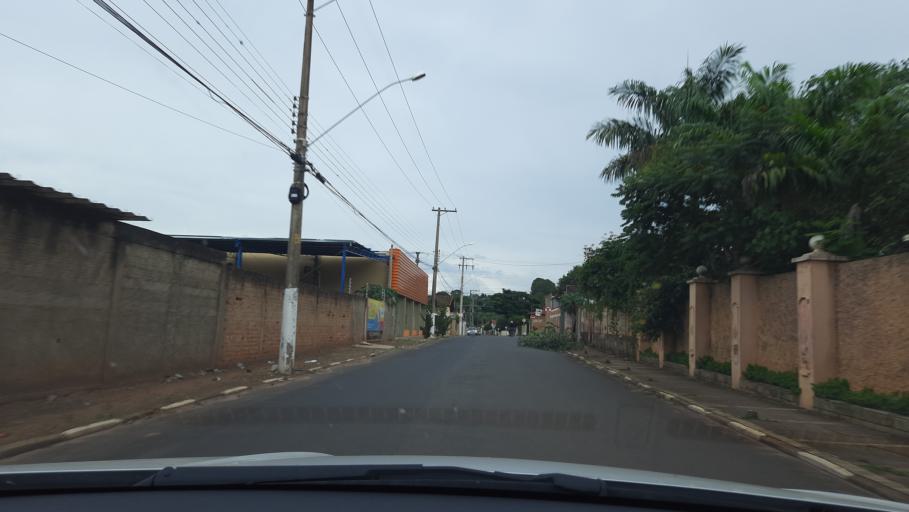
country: BR
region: Sao Paulo
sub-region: Casa Branca
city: Casa Branca
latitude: -21.7692
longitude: -47.0910
